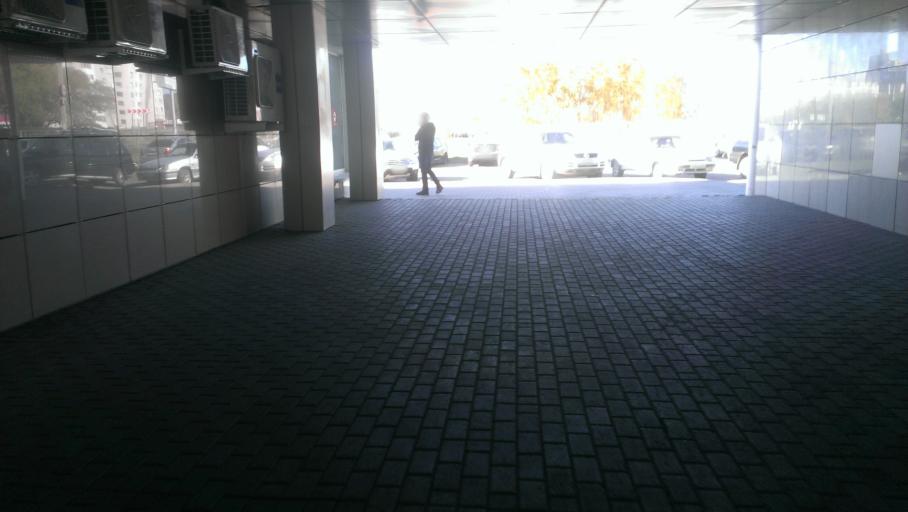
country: RU
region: Altai Krai
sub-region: Gorod Barnaulskiy
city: Barnaul
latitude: 53.3408
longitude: 83.6982
